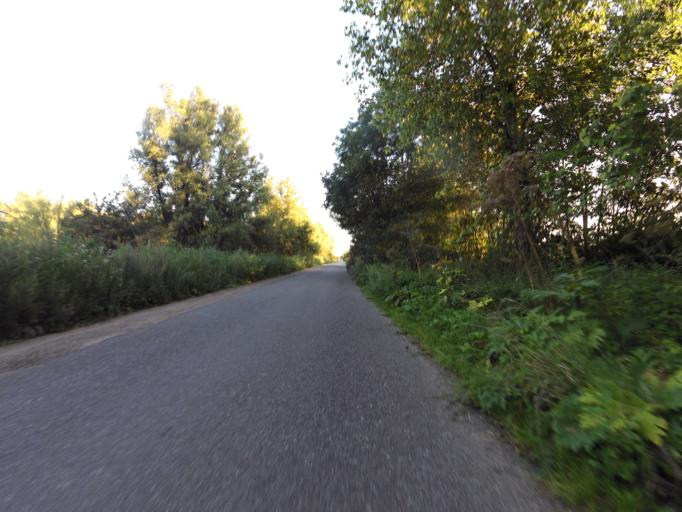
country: NL
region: Gelderland
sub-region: Gemeente Zevenaar
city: Zevenaar
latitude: 51.8827
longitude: 6.0476
